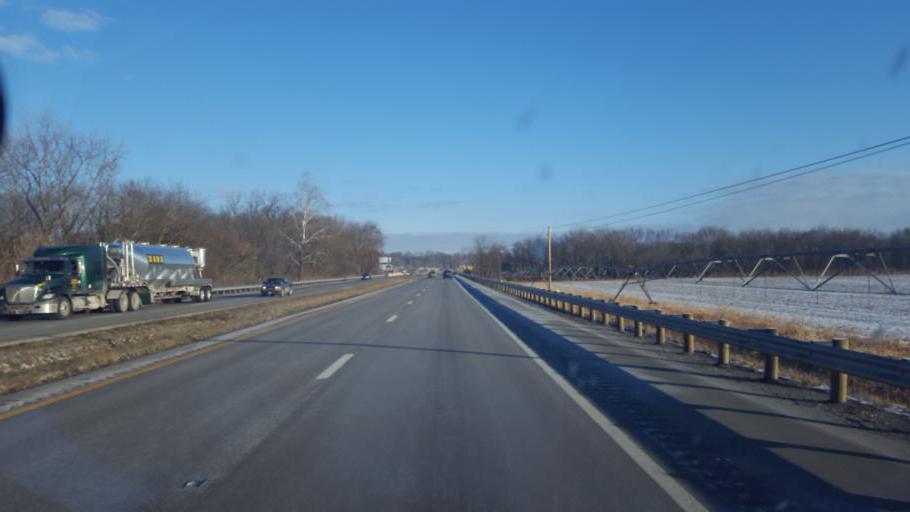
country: US
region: Ohio
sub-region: Pike County
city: Waverly
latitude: 39.1043
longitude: -82.9986
